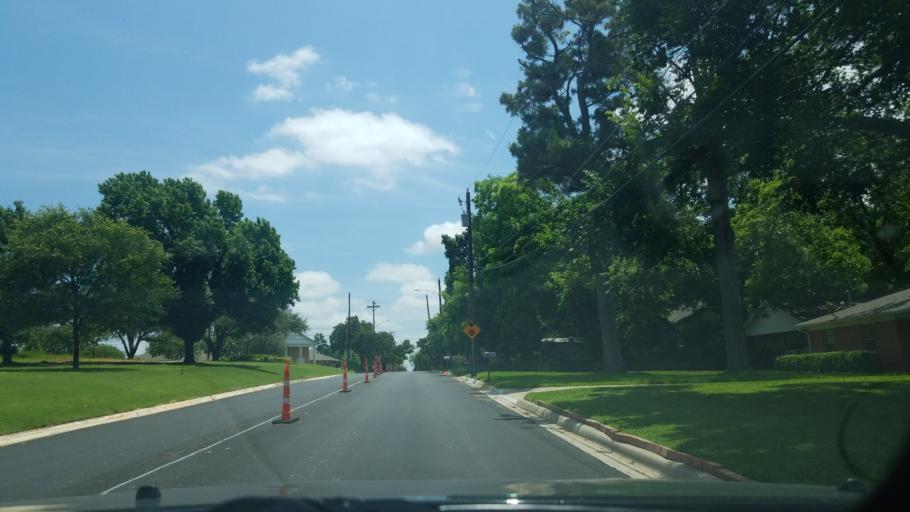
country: US
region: Texas
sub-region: Denton County
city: Denton
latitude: 33.2189
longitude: -97.1601
